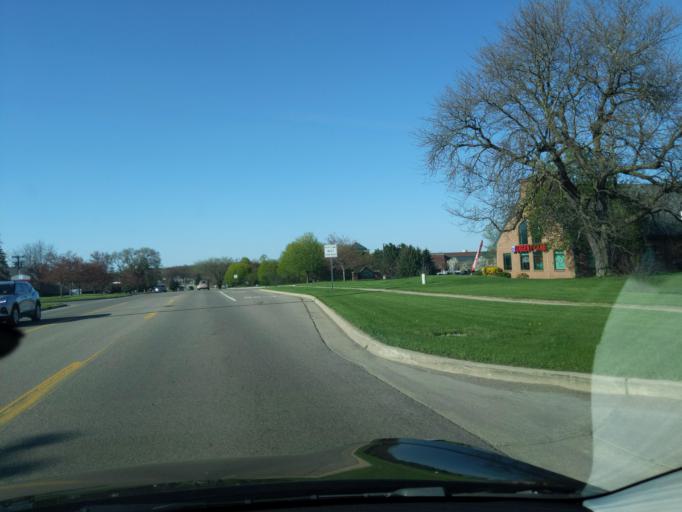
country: US
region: Michigan
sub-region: Washtenaw County
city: Chelsea
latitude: 42.3005
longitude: -84.0238
